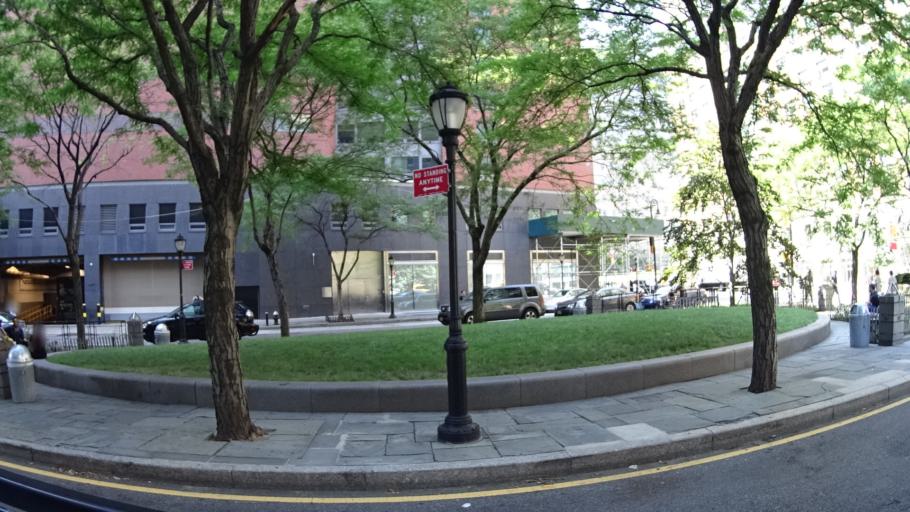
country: US
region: New York
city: New York City
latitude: 40.7156
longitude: -74.0149
